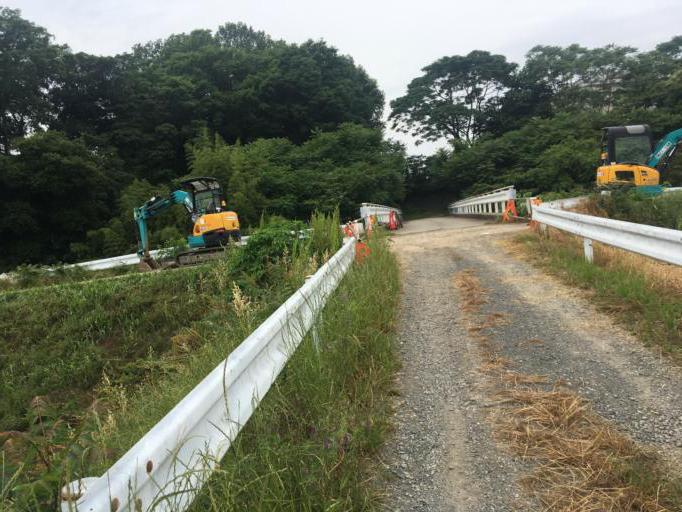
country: JP
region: Saitama
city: Sakado
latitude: 36.0109
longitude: 139.4398
